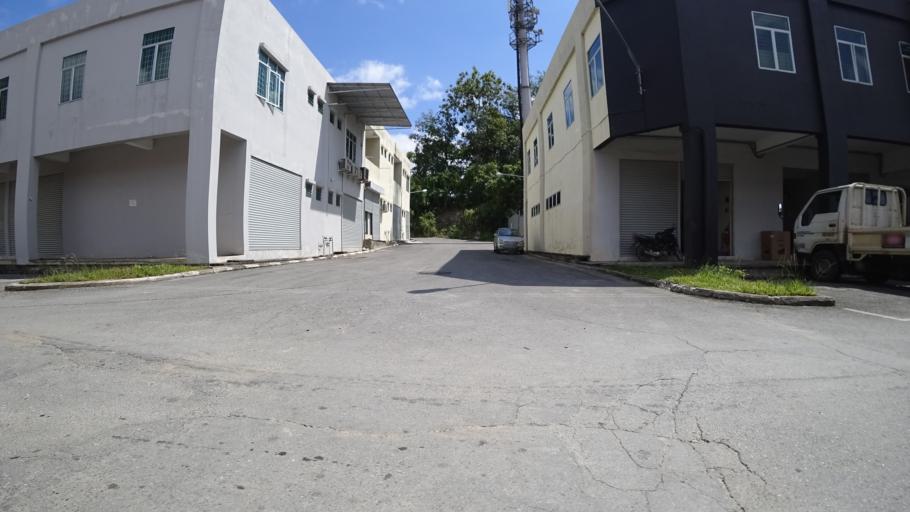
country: MY
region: Sarawak
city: Limbang
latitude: 4.7603
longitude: 115.0065
